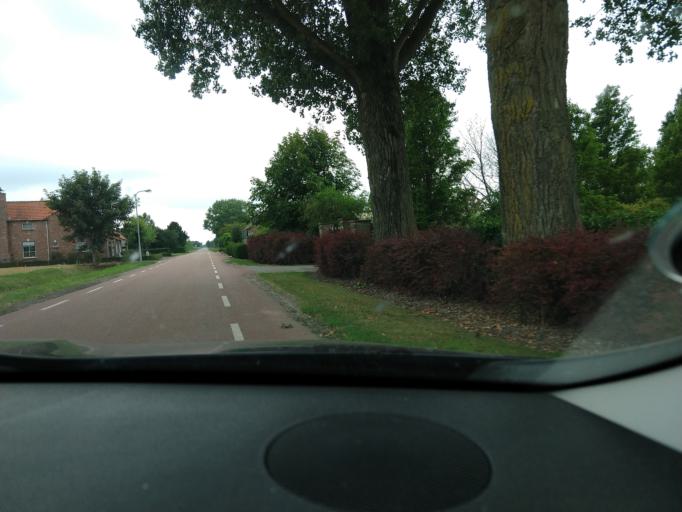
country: NL
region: Zeeland
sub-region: Gemeente Hulst
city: Hulst
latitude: 51.3573
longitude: 4.0586
